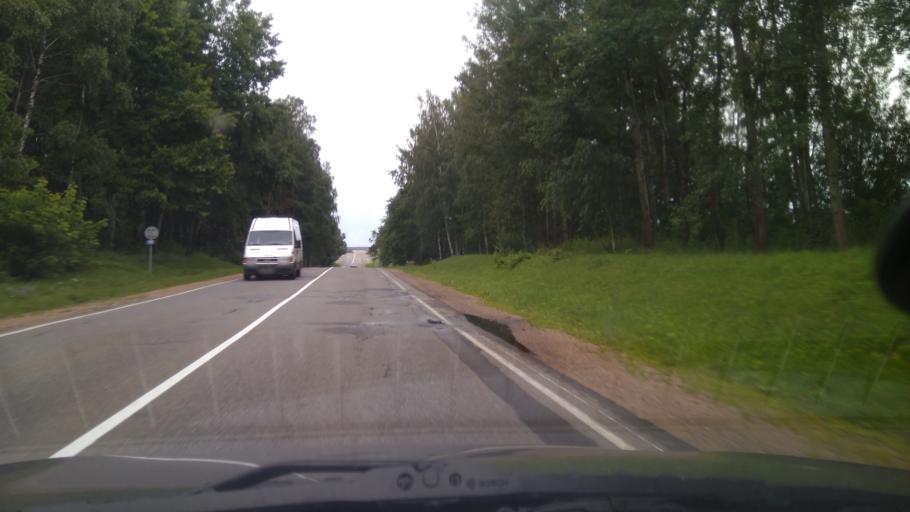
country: BY
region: Minsk
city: Bal'shavik
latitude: 53.9839
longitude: 27.5498
